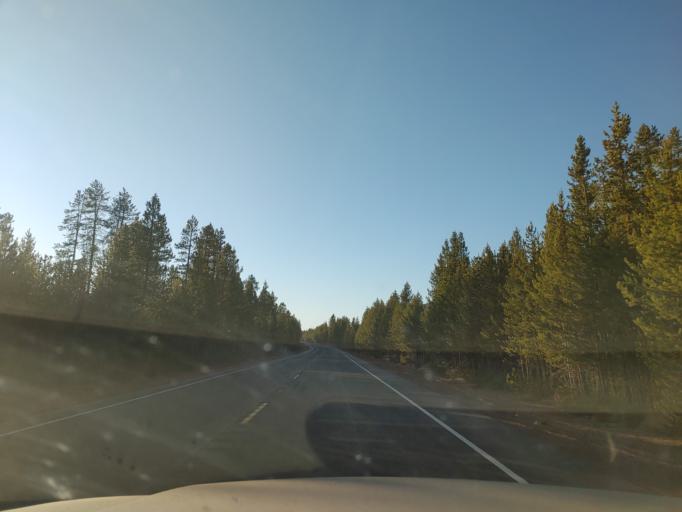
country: US
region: Oregon
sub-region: Deschutes County
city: La Pine
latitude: 43.4191
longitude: -121.8396
